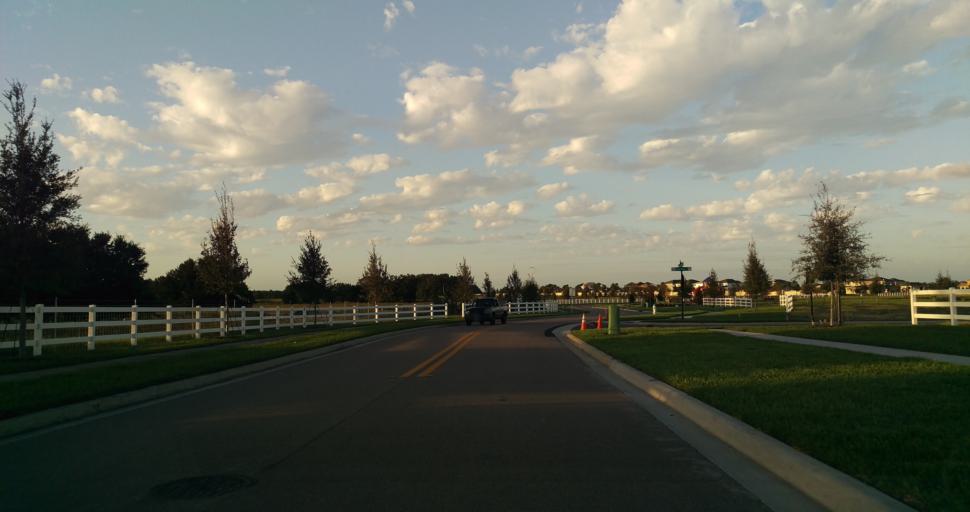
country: US
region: Florida
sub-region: Orange County
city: Lake Butler
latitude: 28.4461
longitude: -81.6236
